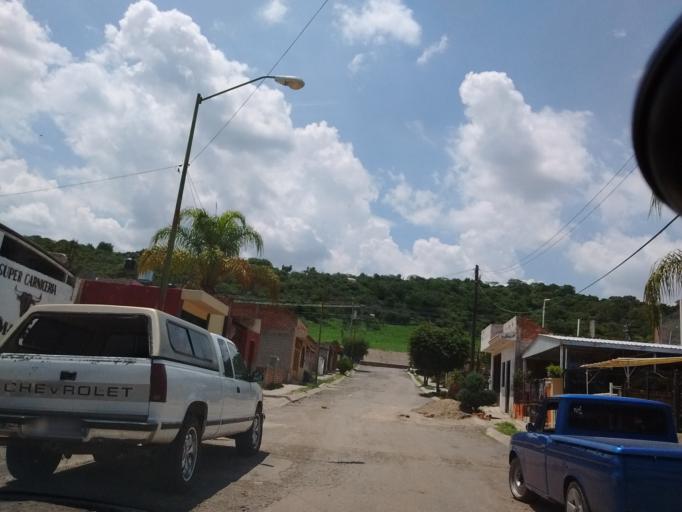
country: MX
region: Jalisco
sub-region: Atotonilco el Alto
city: Vistas del Maguey [Fraccionamiento]
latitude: 20.5278
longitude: -102.5279
